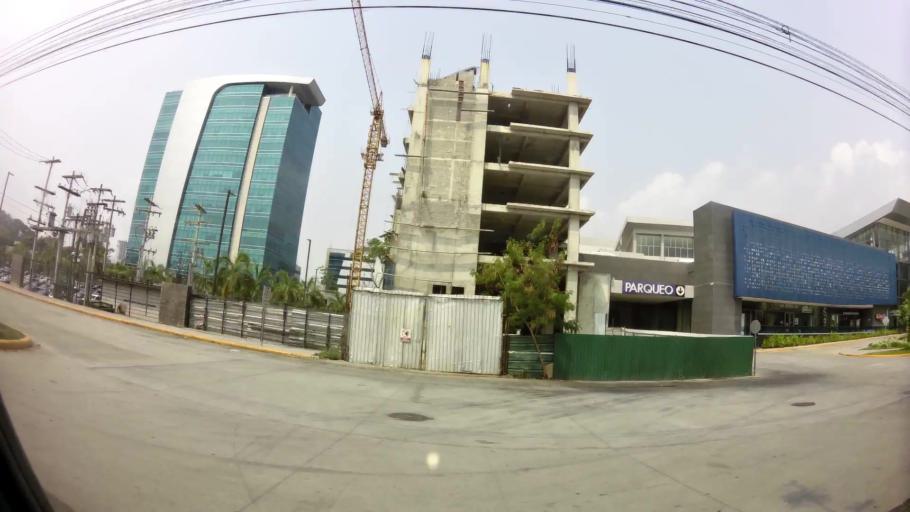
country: HN
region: Cortes
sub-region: San Pedro Sula
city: Pena Blanca
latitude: 15.5627
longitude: -88.0208
